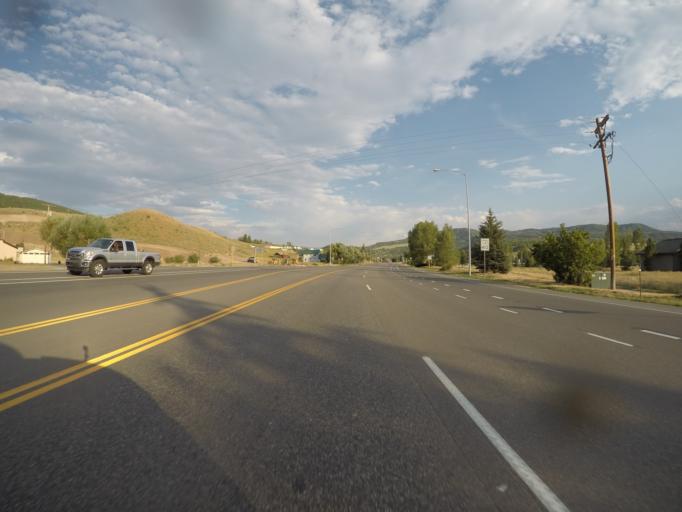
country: US
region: Colorado
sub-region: Routt County
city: Steamboat Springs
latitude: 40.5011
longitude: -106.8555
